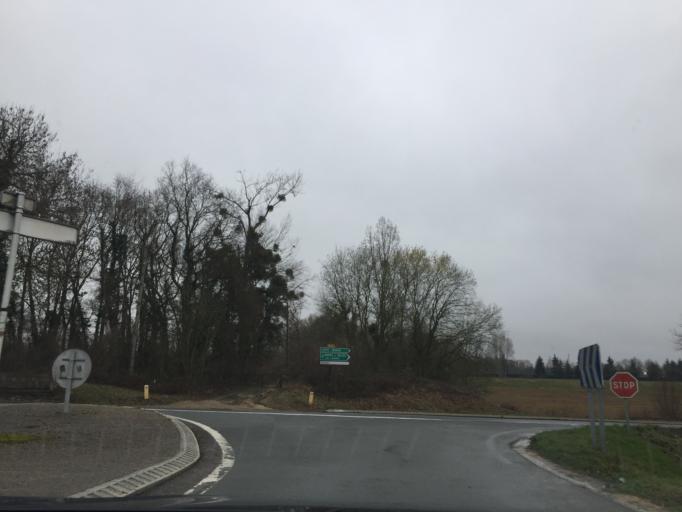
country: FR
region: Ile-de-France
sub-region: Departement de Seine-et-Marne
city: Coupvray
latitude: 48.8829
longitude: 2.7927
